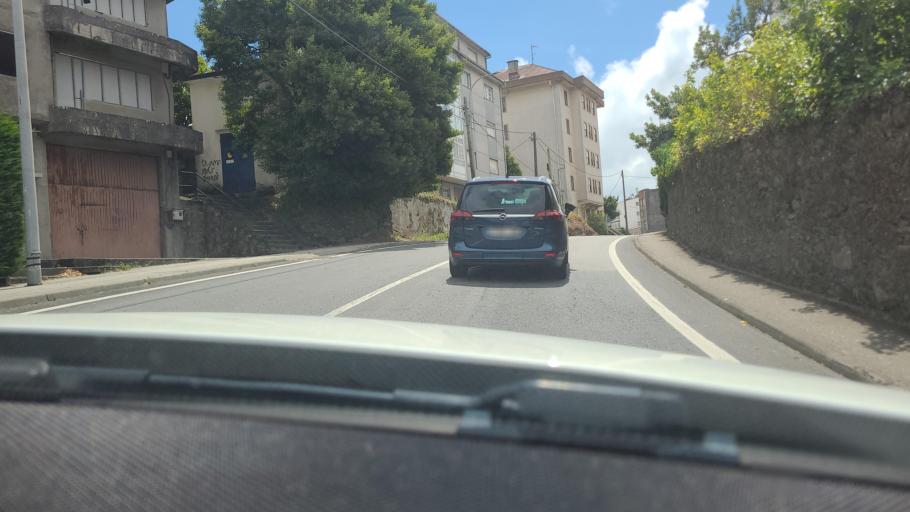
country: ES
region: Galicia
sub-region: Provincia da Coruna
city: Cee
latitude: 42.9544
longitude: -9.1871
